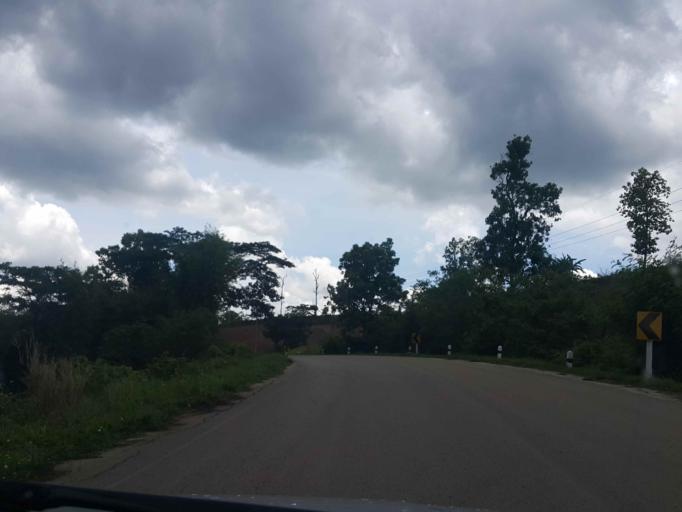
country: TH
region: Phayao
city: Dok Kham Tai
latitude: 18.9664
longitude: 100.0742
